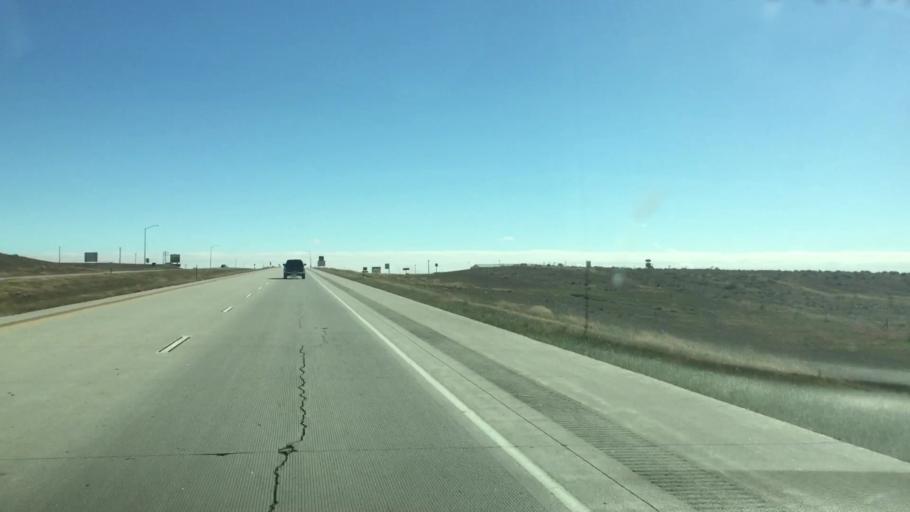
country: US
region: Colorado
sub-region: Lincoln County
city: Limon
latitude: 39.2732
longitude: -103.7218
